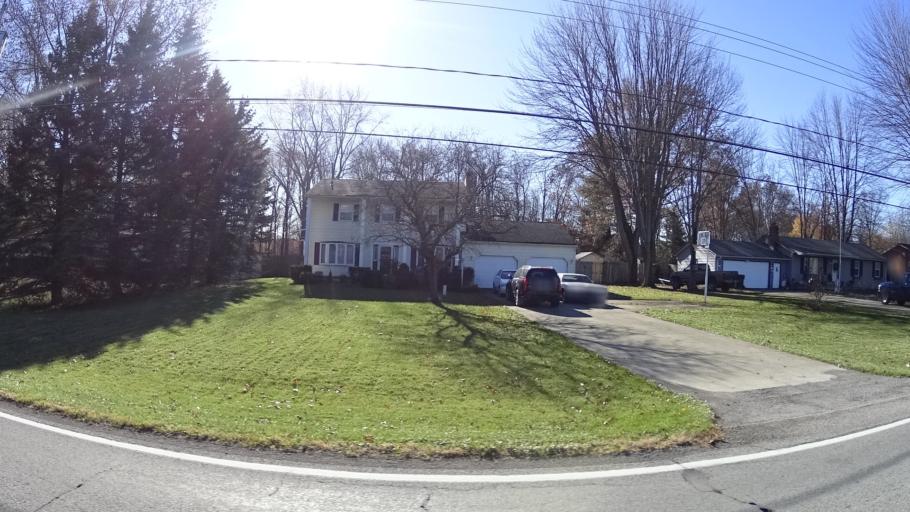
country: US
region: Ohio
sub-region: Lorain County
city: Elyria
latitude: 41.3522
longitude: -82.1527
